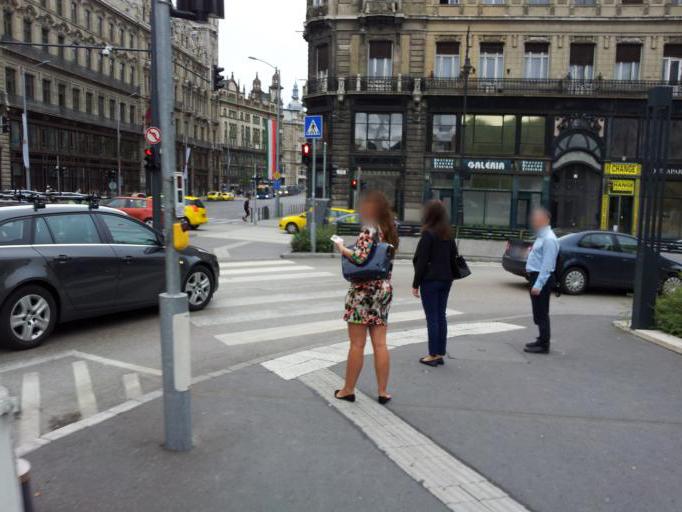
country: HU
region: Budapest
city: Budapest I. keruelet
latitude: 47.4921
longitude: 19.0532
